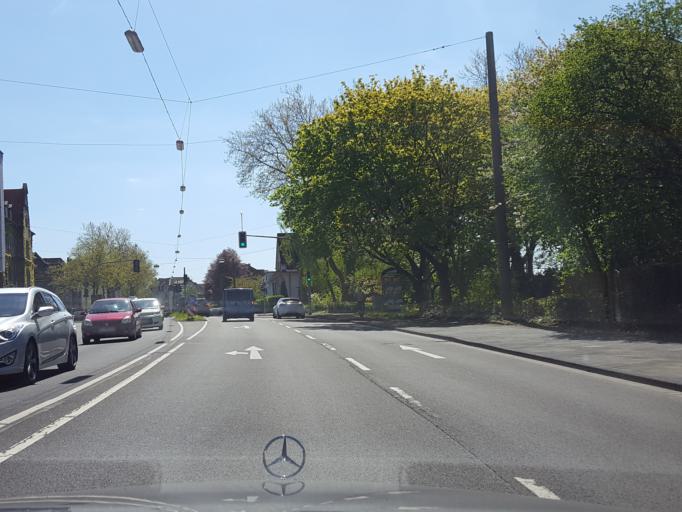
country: DE
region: North Rhine-Westphalia
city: Castrop-Rauxel
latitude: 51.5526
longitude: 7.3121
